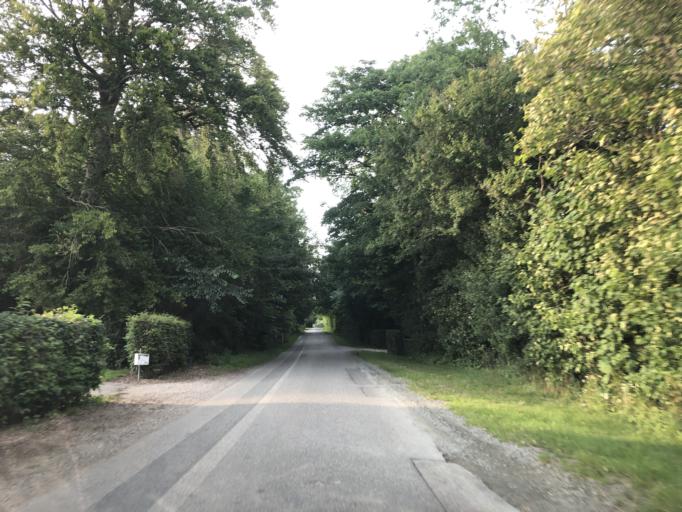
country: DK
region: South Denmark
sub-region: Fredericia Kommune
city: Taulov
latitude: 55.5989
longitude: 9.6020
